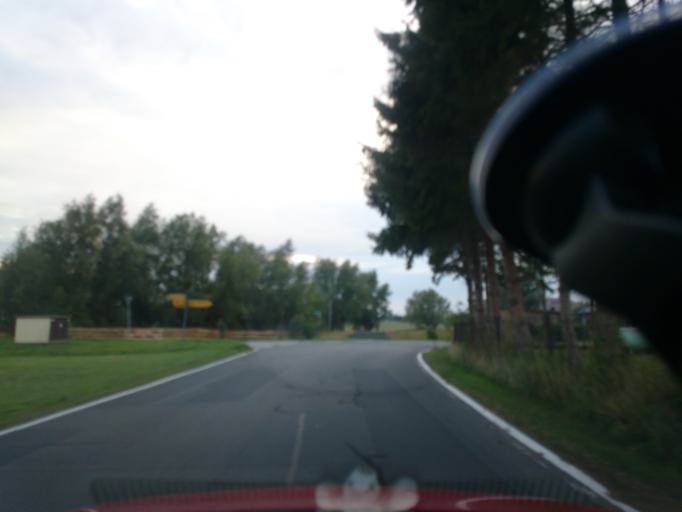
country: DE
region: Mecklenburg-Vorpommern
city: Saal
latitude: 54.3311
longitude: 12.5266
